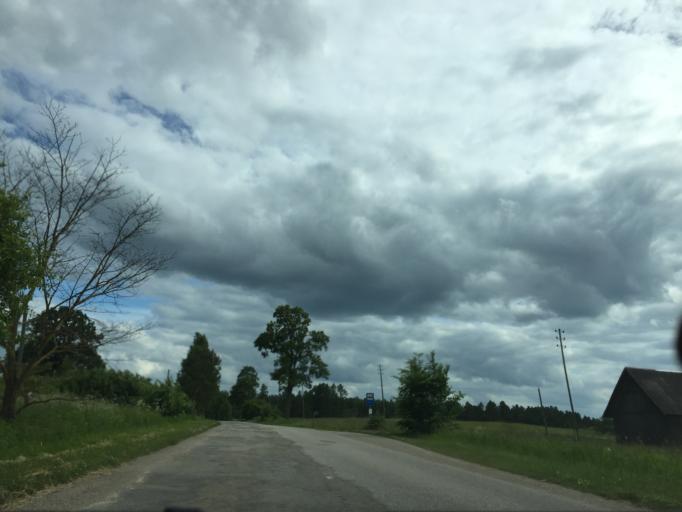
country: LV
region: Apes Novads
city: Ape
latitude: 57.5033
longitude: 26.4007
